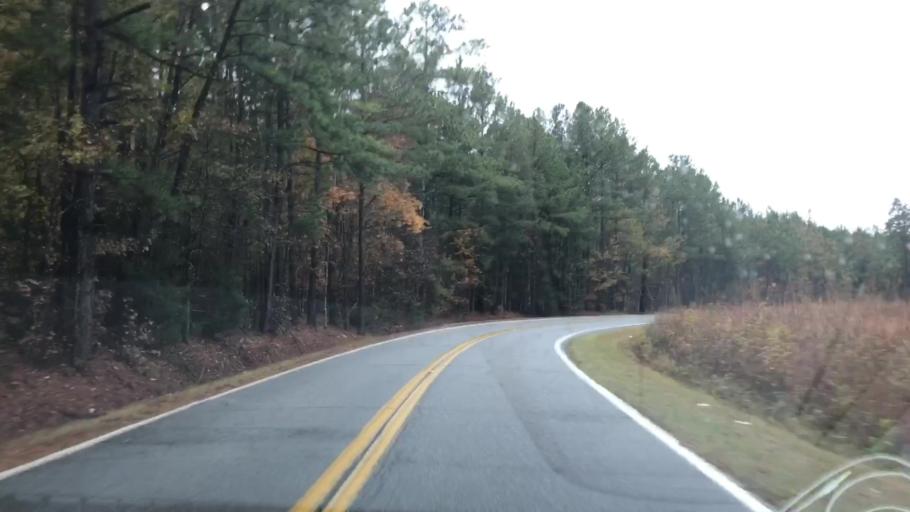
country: US
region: South Carolina
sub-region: Greenwood County
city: Ninety Six
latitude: 34.2905
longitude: -81.9749
